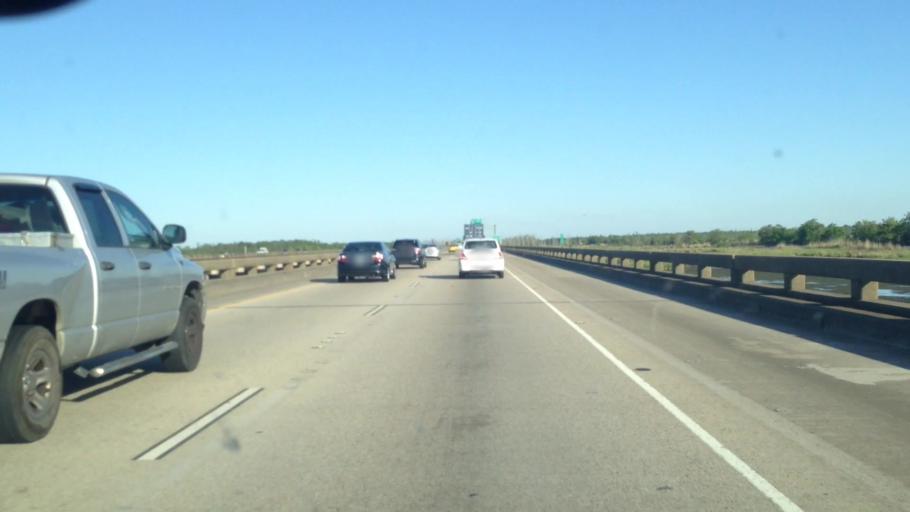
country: US
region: Louisiana
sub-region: Saint Charles Parish
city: Ama
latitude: 30.0168
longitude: -90.3150
